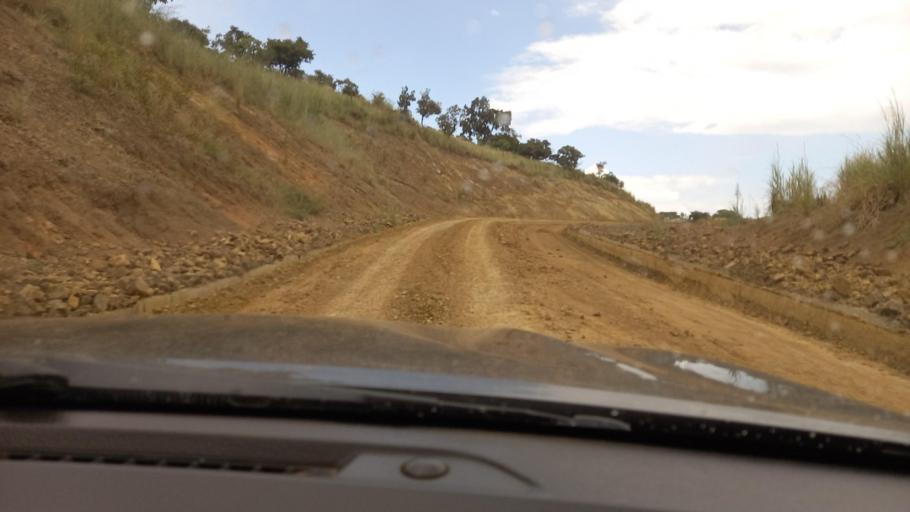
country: ET
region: Southern Nations, Nationalities, and People's Region
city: Mizan Teferi
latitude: 6.2064
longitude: 35.6711
